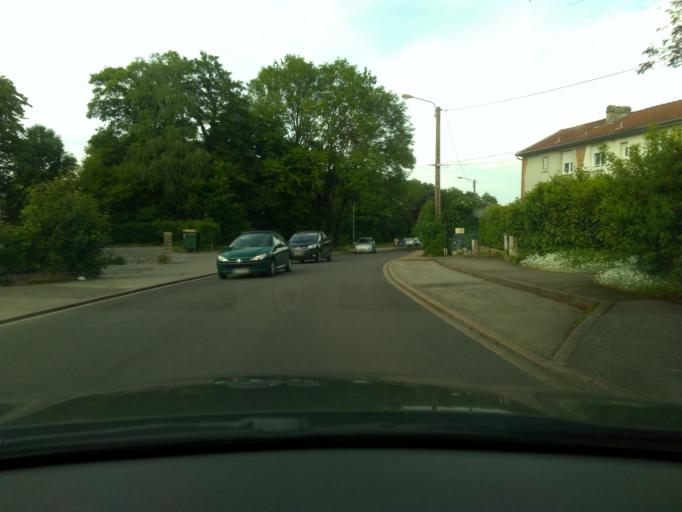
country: FR
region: Lorraine
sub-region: Departement de la Moselle
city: Seremange-Erzange
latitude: 49.3147
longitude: 6.0772
